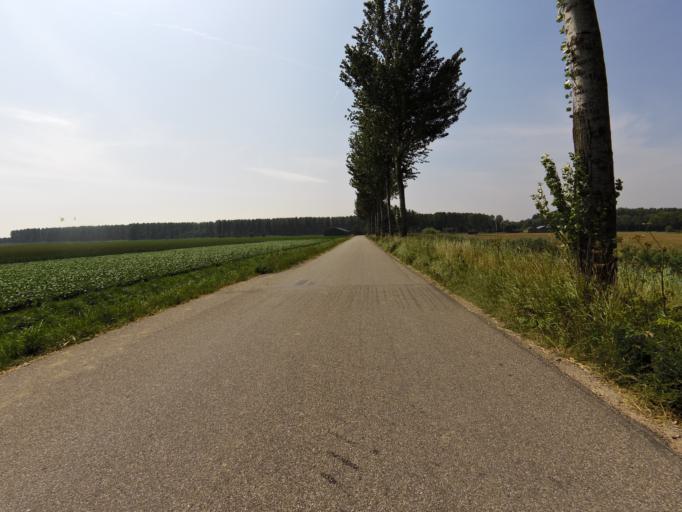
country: NL
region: South Holland
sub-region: Gemeente Dordrecht
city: Dordrecht
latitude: 51.7617
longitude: 4.7018
